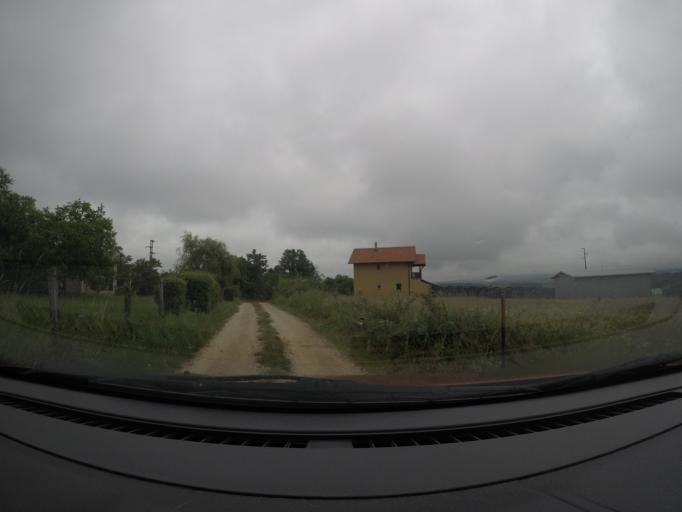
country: RS
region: Central Serbia
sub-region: Belgrade
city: Sopot
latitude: 44.5200
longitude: 20.5371
